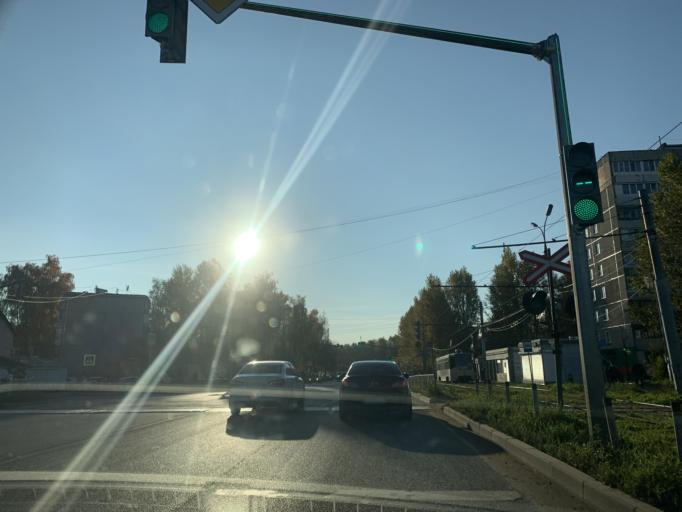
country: RU
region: Jaroslavl
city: Yaroslavl
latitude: 57.6846
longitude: 39.7686
